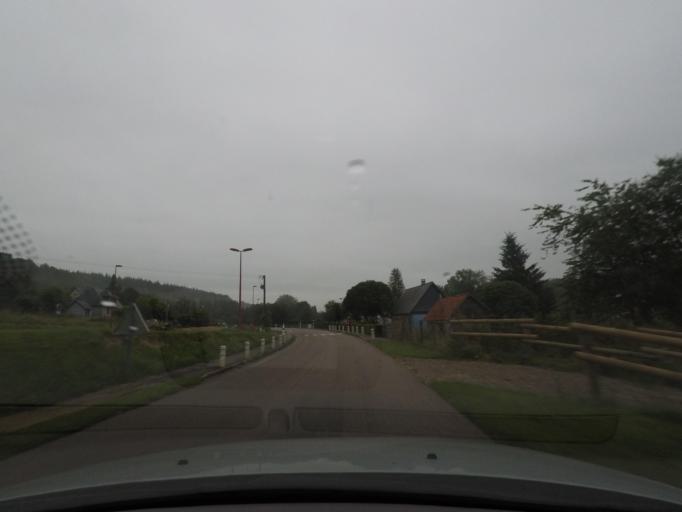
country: FR
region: Haute-Normandie
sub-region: Departement de la Seine-Maritime
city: Fontaine-le-Bourg
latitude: 49.5781
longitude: 1.2078
